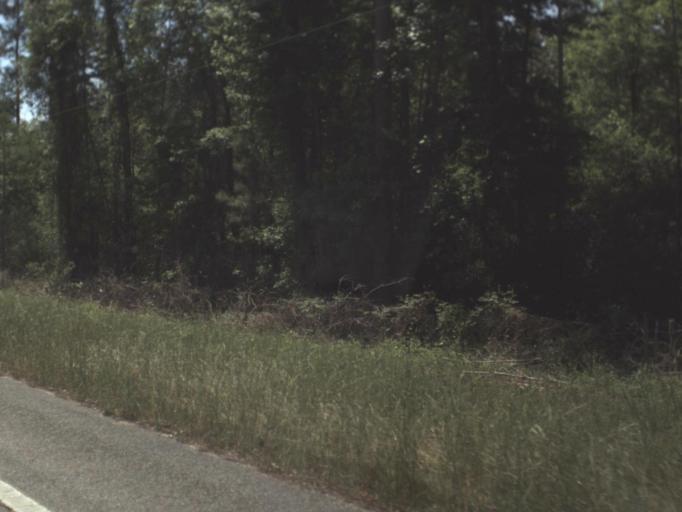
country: US
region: Florida
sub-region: Jackson County
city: Marianna
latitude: 30.6622
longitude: -85.2234
